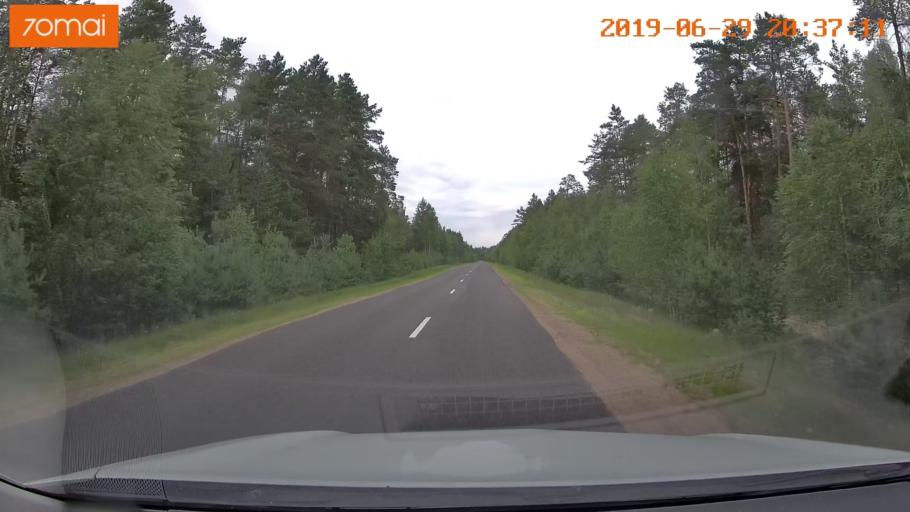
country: BY
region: Brest
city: Hantsavichy
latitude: 52.5348
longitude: 26.3635
